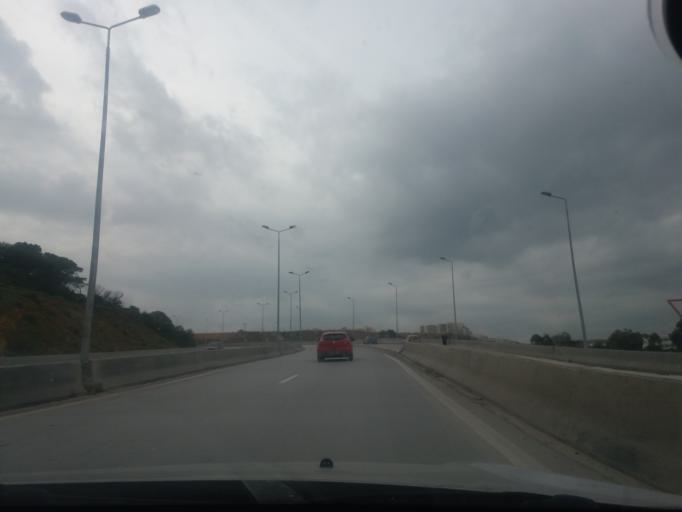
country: TN
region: Ariana
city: Ariana
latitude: 36.8660
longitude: 10.1812
